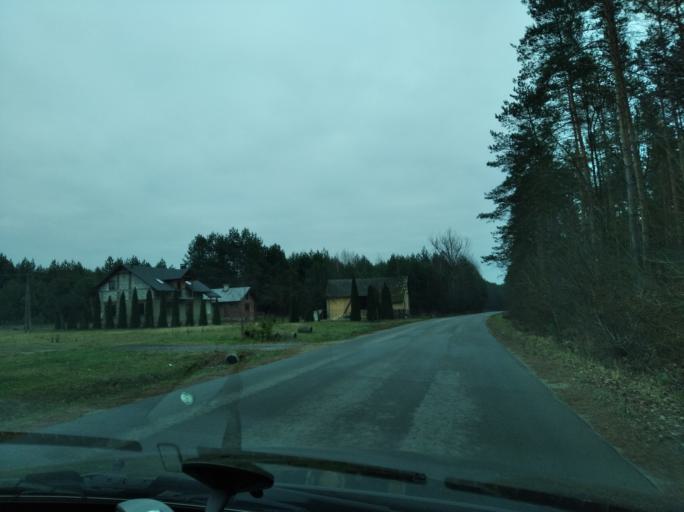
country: PL
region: Subcarpathian Voivodeship
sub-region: Powiat lancucki
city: Czarna
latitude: 50.1612
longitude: 22.1785
